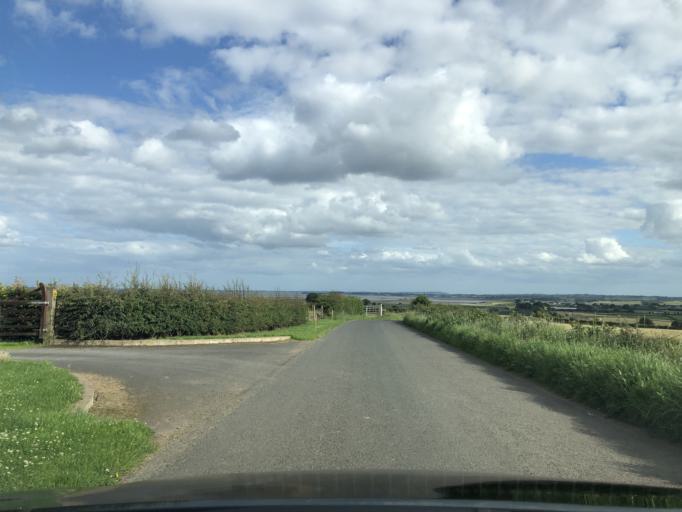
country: GB
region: Northern Ireland
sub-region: Ards District
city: Newtownards
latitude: 54.5720
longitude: -5.7147
